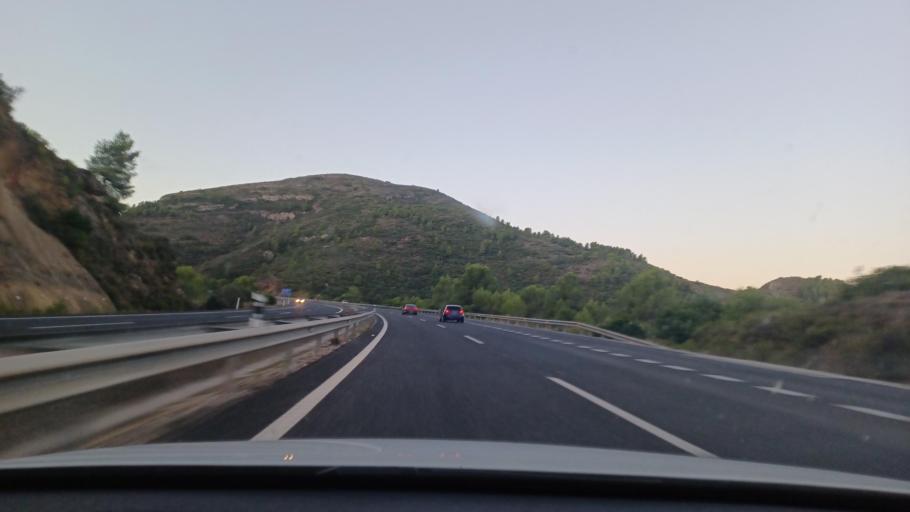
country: ES
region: Valencia
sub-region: Provincia de Alicante
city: Senija
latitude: 38.7597
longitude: 0.0532
